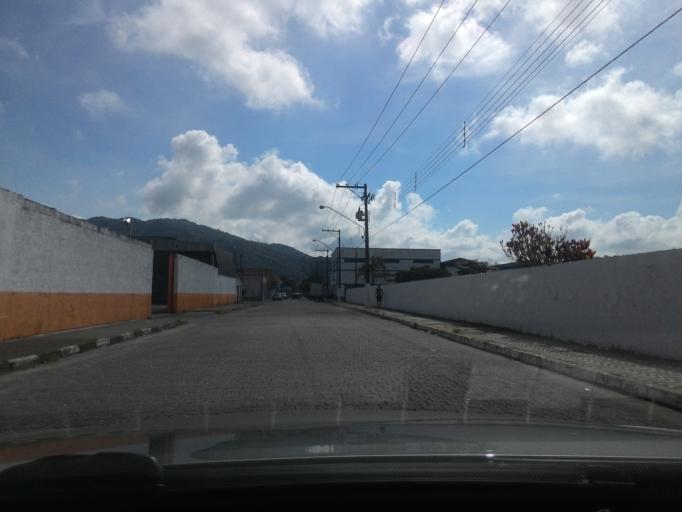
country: BR
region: Sao Paulo
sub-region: Iguape
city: Iguape
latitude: -24.7122
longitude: -47.5617
